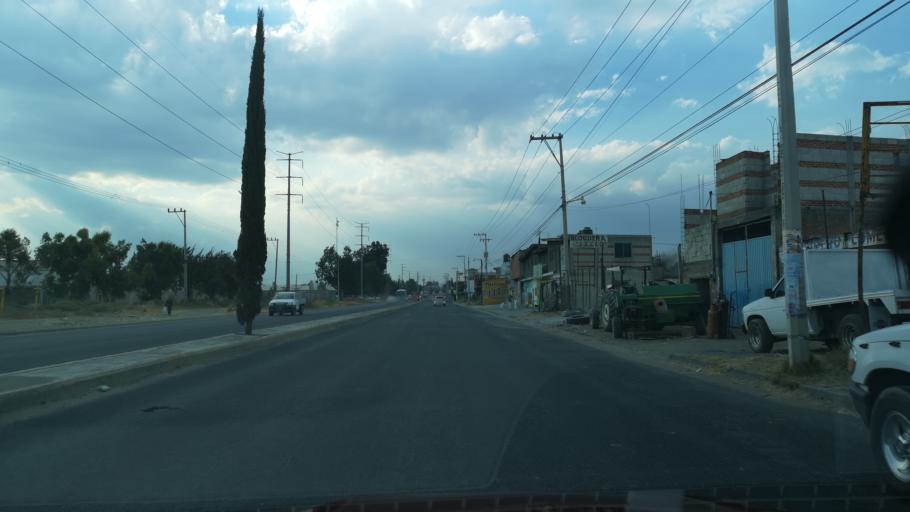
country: MX
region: Puebla
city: Cuanala
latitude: 19.0917
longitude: -98.3372
